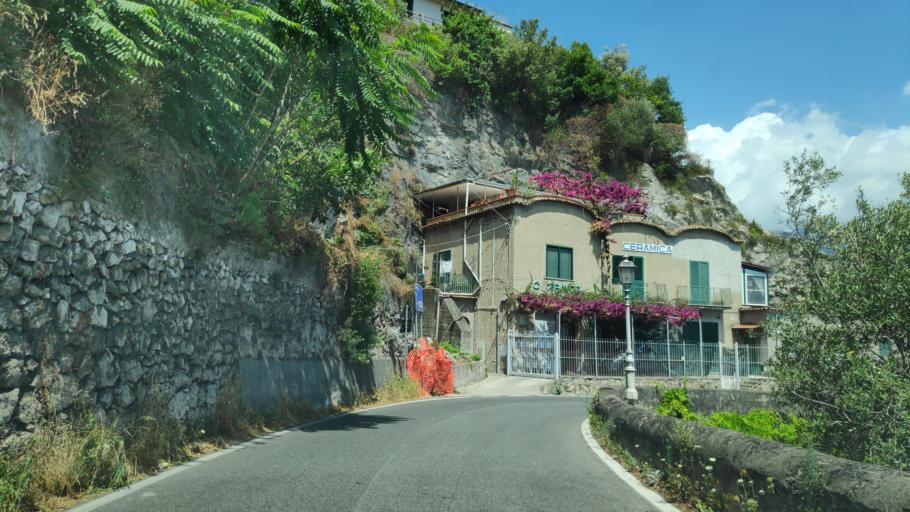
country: IT
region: Campania
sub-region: Provincia di Salerno
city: Atrani
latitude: 40.6397
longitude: 14.6135
